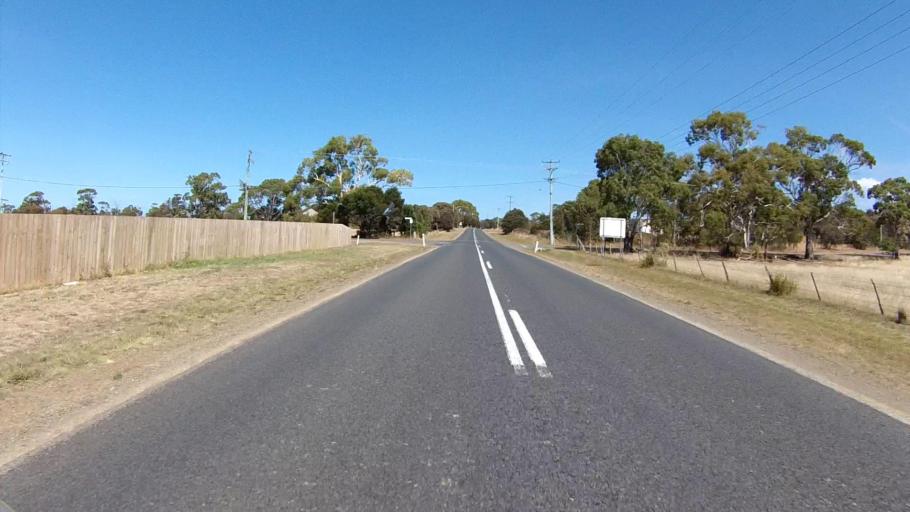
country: AU
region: Tasmania
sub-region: Sorell
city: Sorell
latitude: -42.1371
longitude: 148.0710
